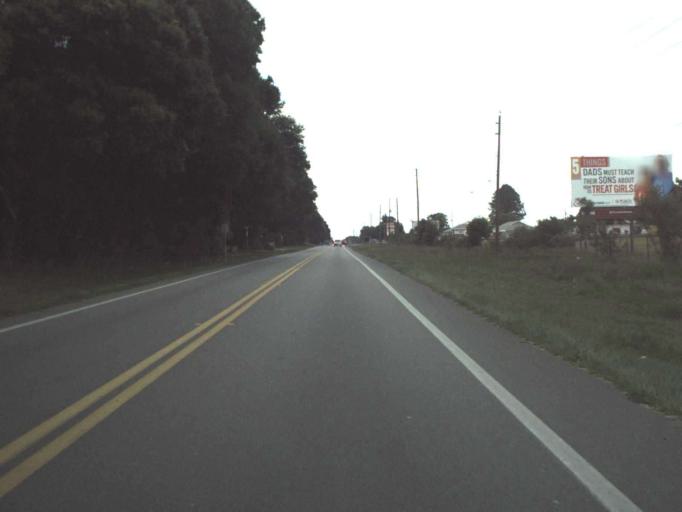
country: US
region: Florida
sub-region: Marion County
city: Belleview
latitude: 29.0746
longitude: -82.0535
